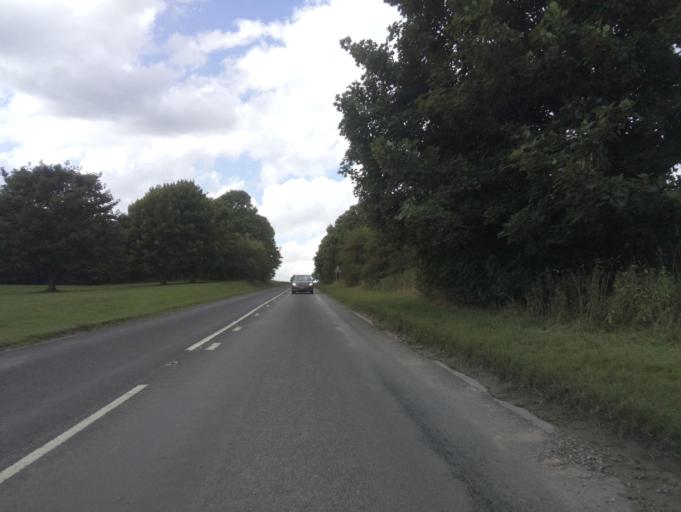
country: GB
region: England
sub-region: North Yorkshire
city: Ripon
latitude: 54.1772
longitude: -1.5548
